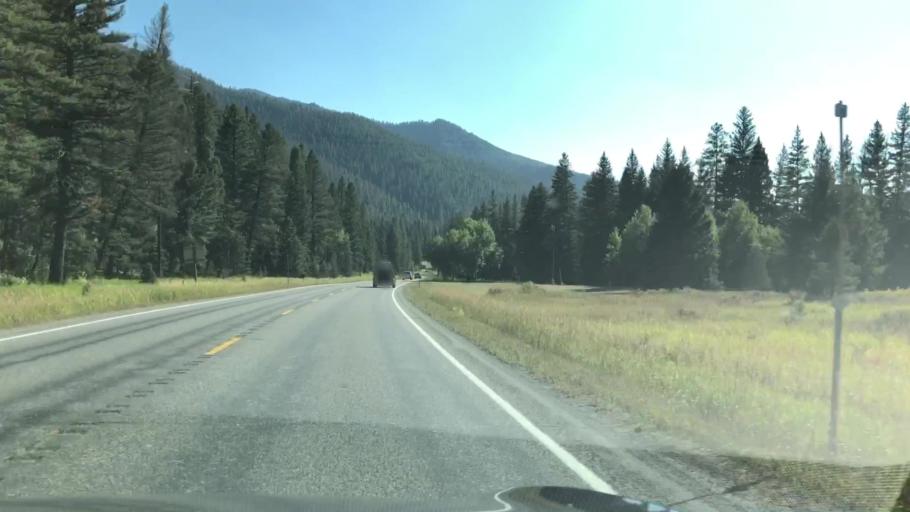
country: US
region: Montana
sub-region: Gallatin County
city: Big Sky
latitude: 45.3285
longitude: -111.1727
